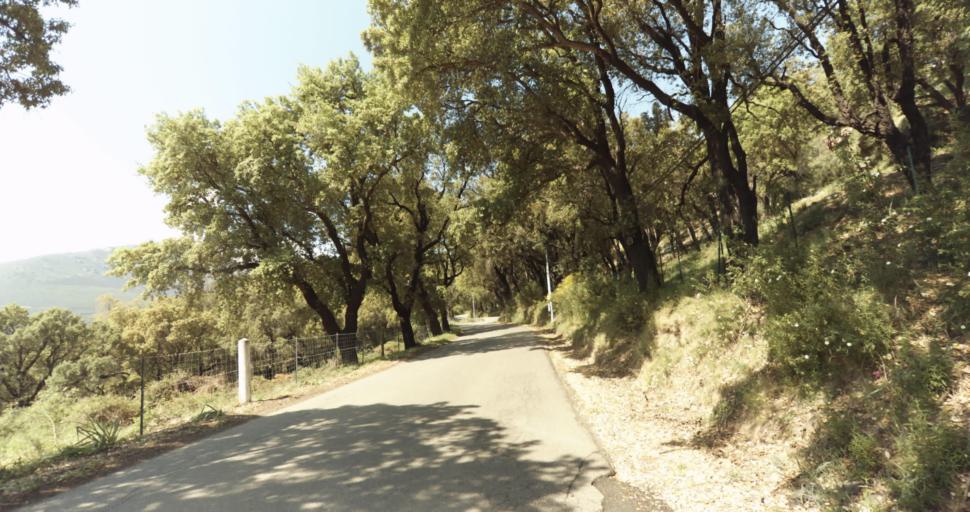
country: FR
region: Corsica
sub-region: Departement de la Haute-Corse
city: Biguglia
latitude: 42.6136
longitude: 9.4164
